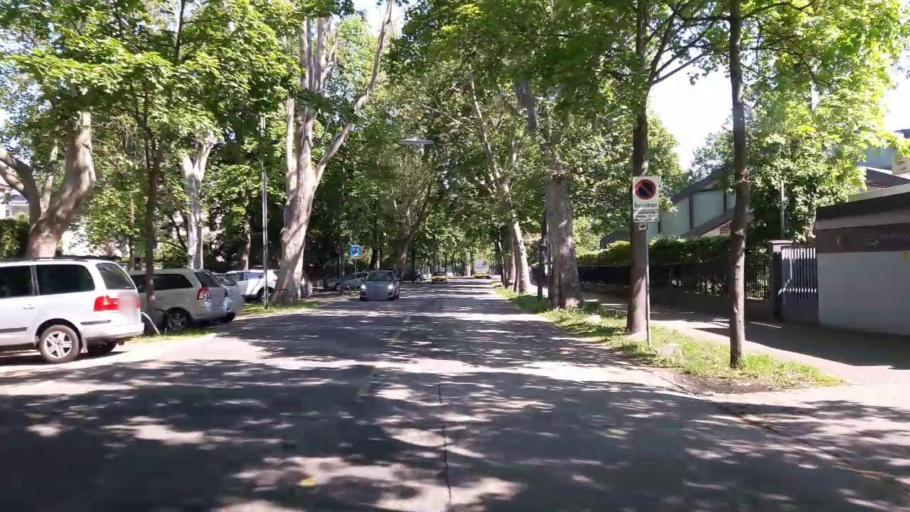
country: AT
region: Vienna
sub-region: Wien Stadt
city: Vienna
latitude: 48.2095
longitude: 16.3989
